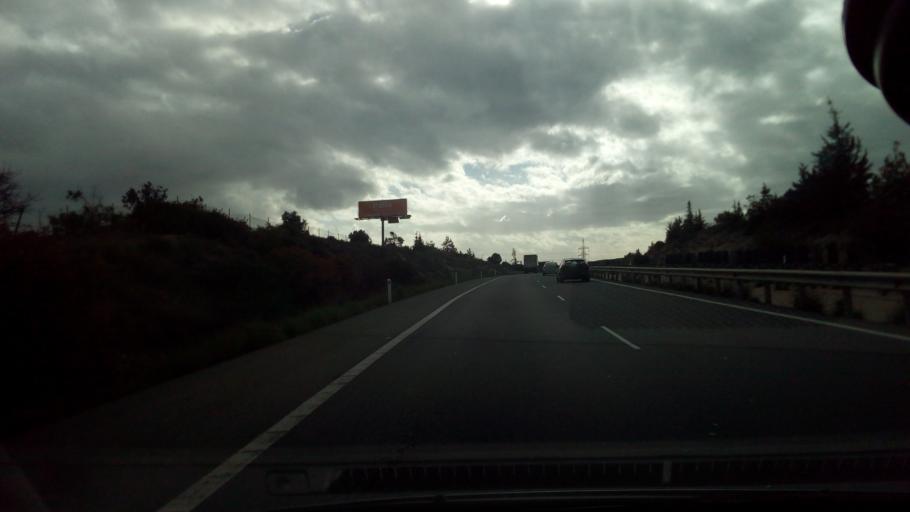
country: CY
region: Limassol
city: Pyrgos
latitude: 34.7337
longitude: 33.2830
